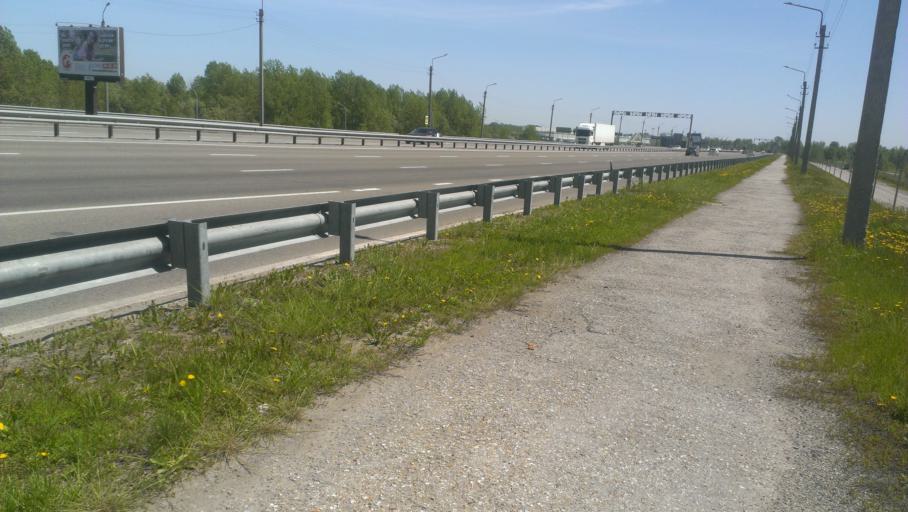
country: RU
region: Altai Krai
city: Zaton
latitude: 53.3189
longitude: 83.8156
